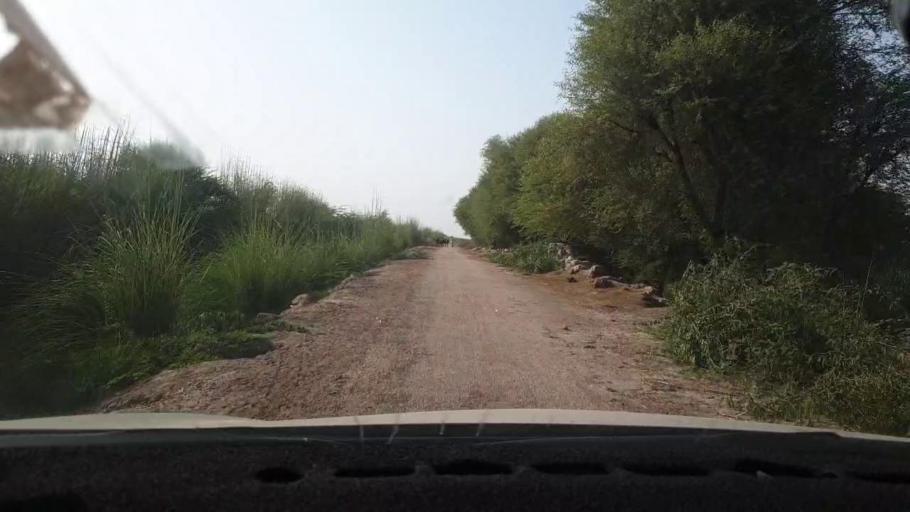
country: PK
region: Sindh
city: Berani
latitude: 25.7543
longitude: 68.7988
